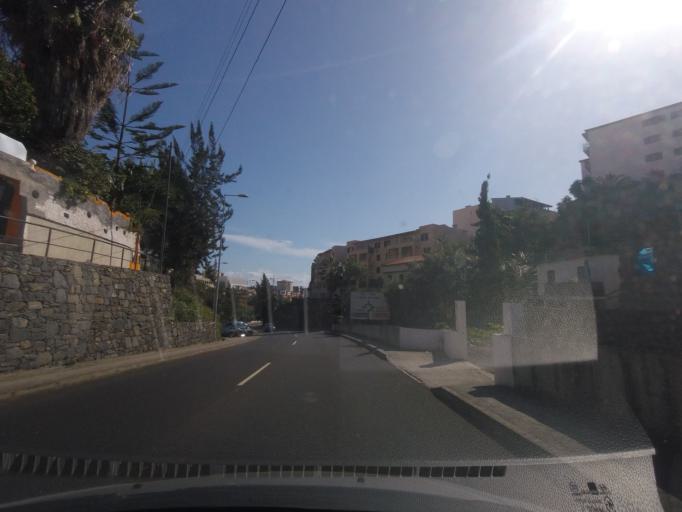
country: PT
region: Madeira
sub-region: Funchal
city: Funchal
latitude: 32.6483
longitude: -16.9259
